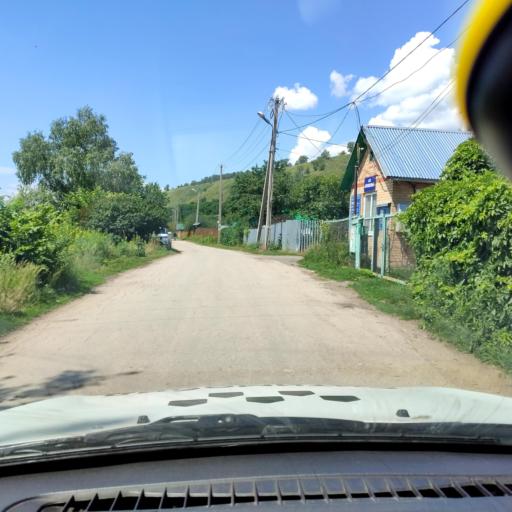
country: RU
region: Samara
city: Povolzhskiy
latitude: 53.4712
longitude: 49.6813
